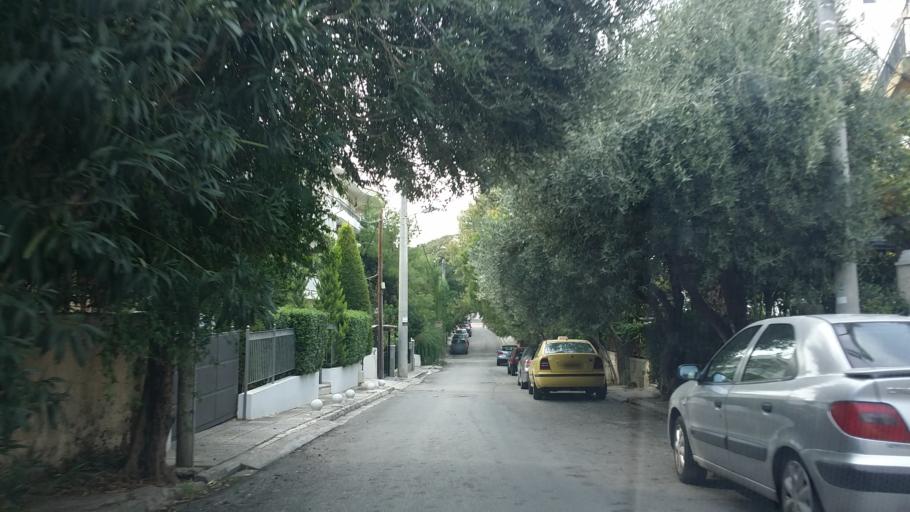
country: GR
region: Attica
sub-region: Nomarchia Athinas
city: Filothei
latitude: 38.0332
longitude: 23.7874
